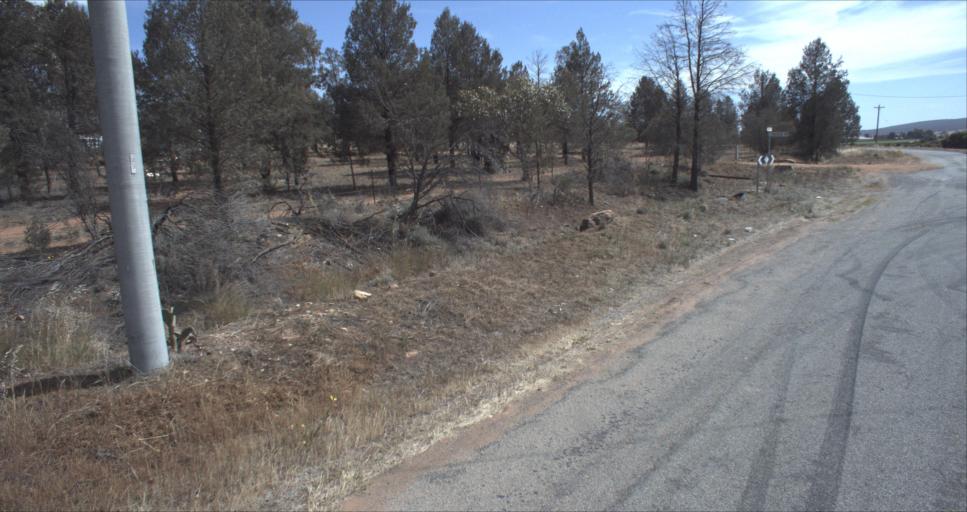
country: AU
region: New South Wales
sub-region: Leeton
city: Leeton
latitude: -34.5700
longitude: 146.4639
